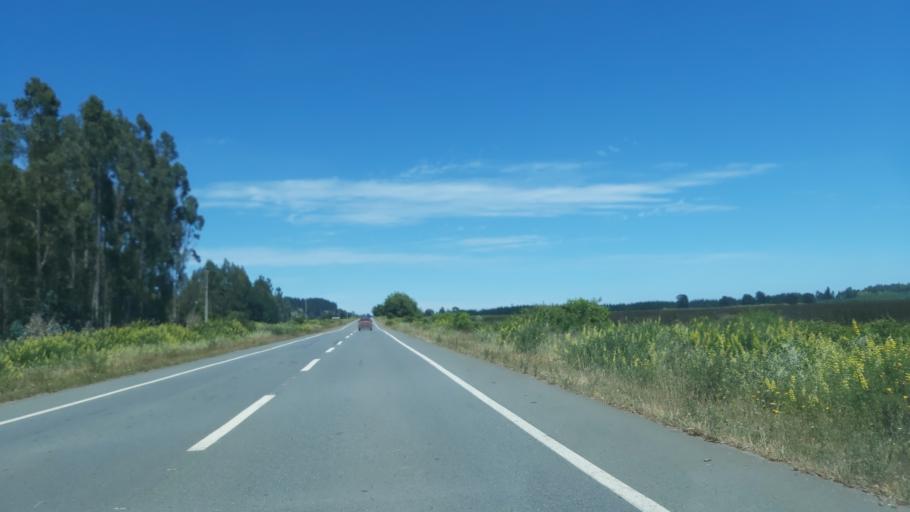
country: CL
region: Maule
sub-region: Provincia de Talca
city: Constitucion
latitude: -35.1604
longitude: -72.2546
